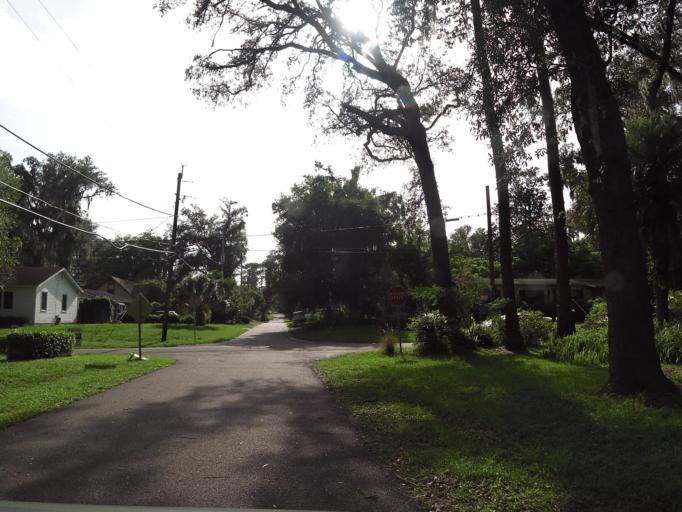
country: US
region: Florida
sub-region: Duval County
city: Jacksonville
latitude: 30.2939
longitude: -81.7239
